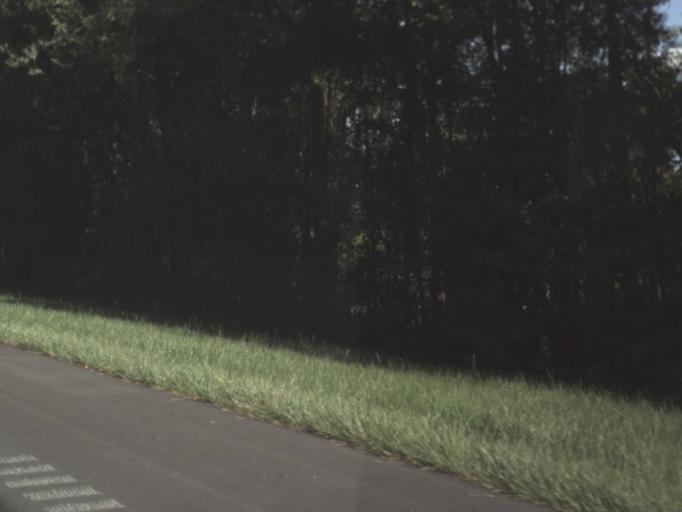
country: US
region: Florida
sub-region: Madison County
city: Madison
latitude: 30.4065
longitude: -83.4027
